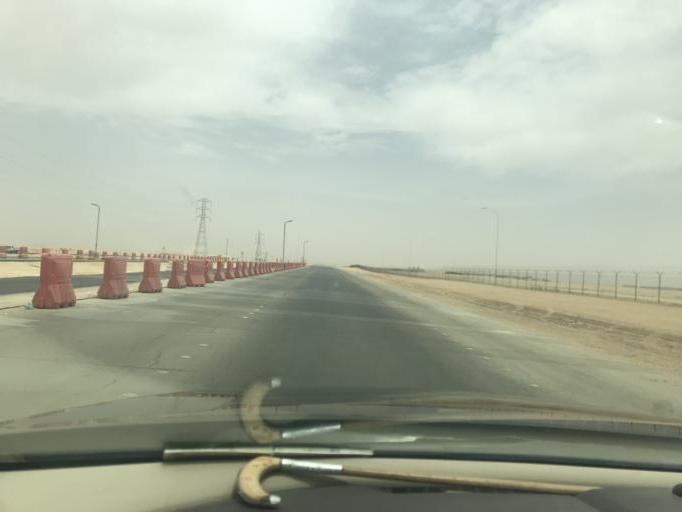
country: SA
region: Ar Riyad
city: Riyadh
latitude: 24.9478
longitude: 46.6773
